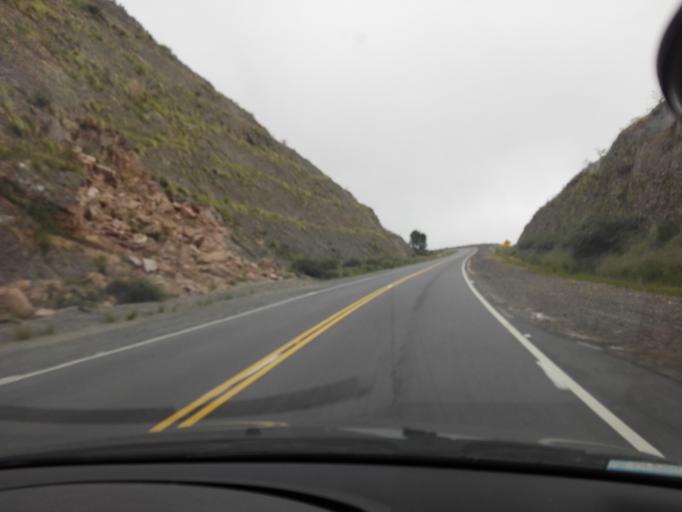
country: AR
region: Cordoba
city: Cuesta Blanca
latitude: -31.6139
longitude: -64.6924
